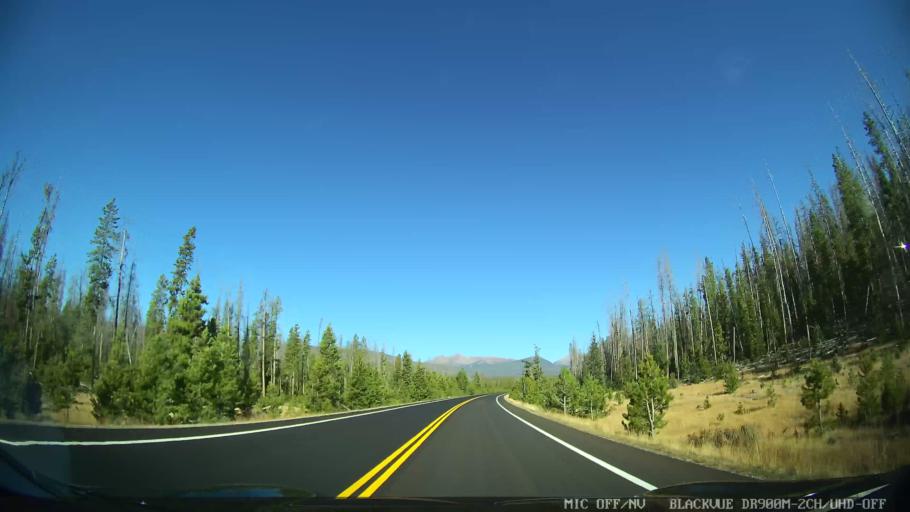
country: US
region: Colorado
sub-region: Grand County
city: Granby
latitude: 40.2831
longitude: -105.8393
